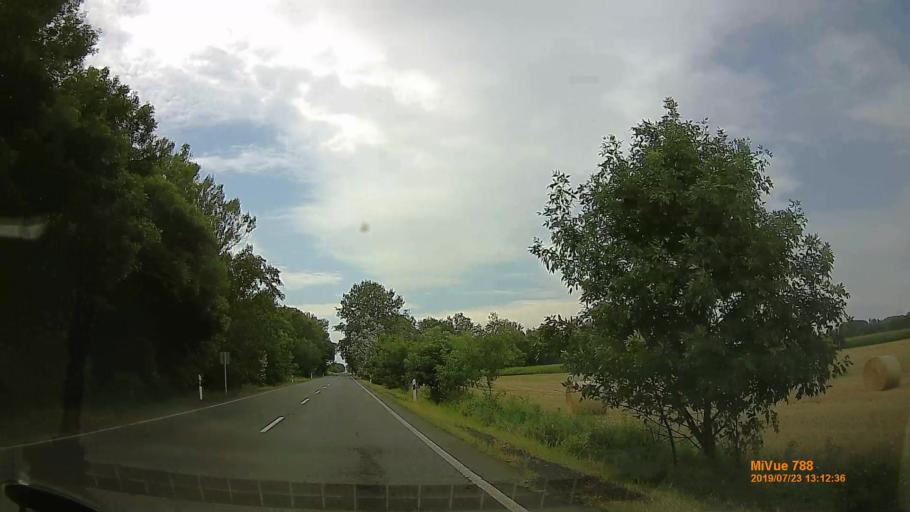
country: HU
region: Hajdu-Bihar
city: Gorbehaza
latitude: 47.9296
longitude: 21.2482
